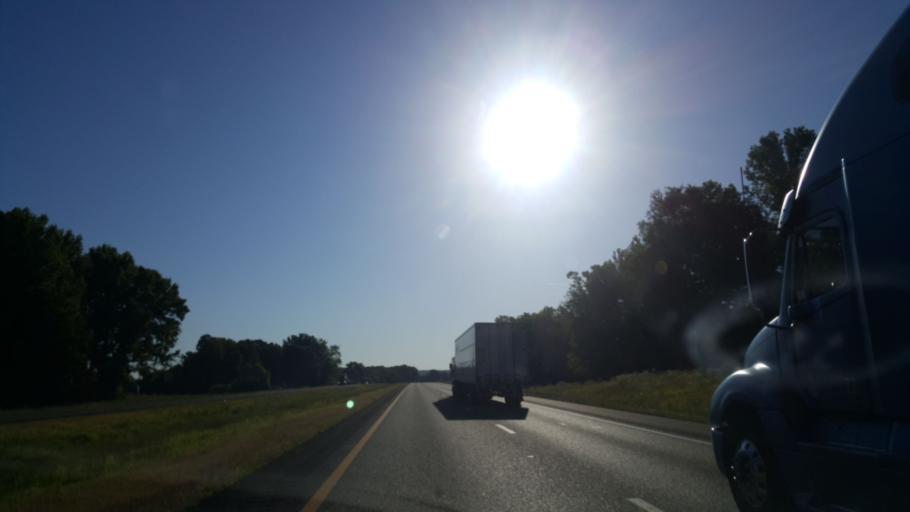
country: US
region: Tennessee
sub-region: Henderson County
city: Lexington
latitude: 35.7955
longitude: -88.3690
